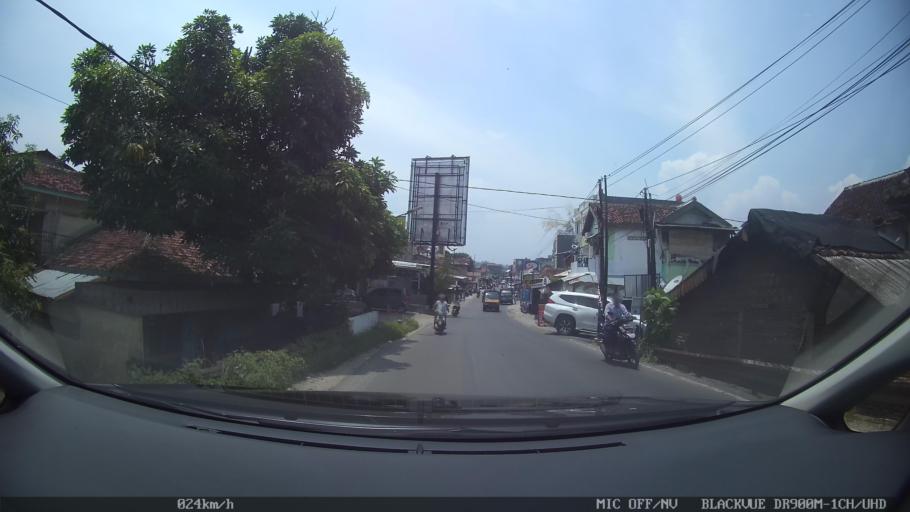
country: ID
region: Lampung
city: Bandarlampung
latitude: -5.4531
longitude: 105.2579
